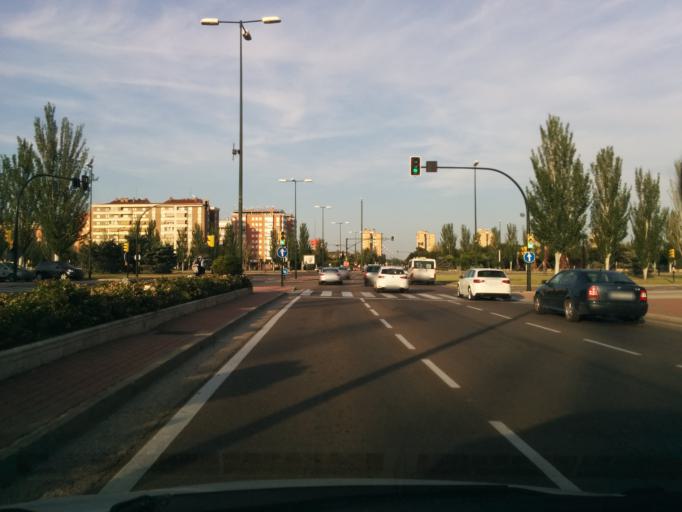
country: ES
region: Aragon
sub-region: Provincia de Zaragoza
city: Zaragoza
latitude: 41.6665
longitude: -0.8819
